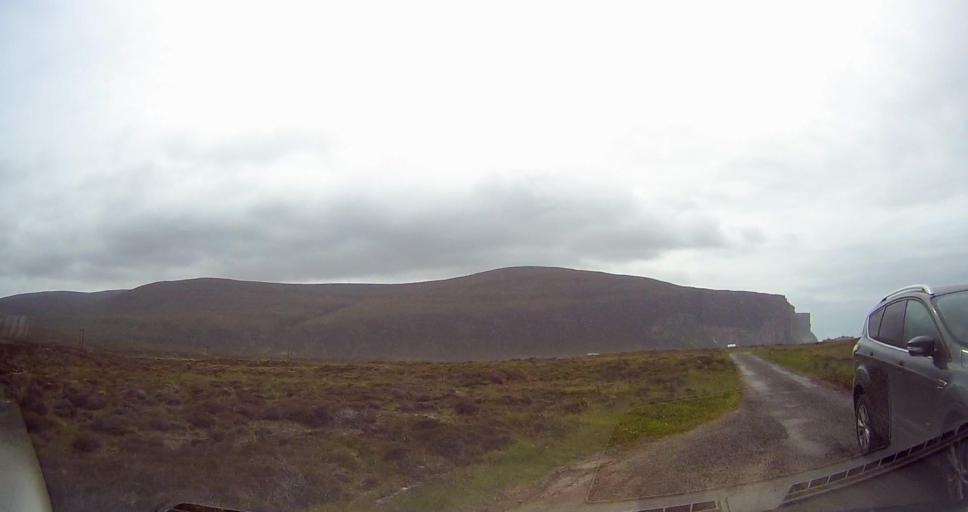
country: GB
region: Scotland
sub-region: Orkney Islands
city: Stromness
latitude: 58.8749
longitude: -3.3867
